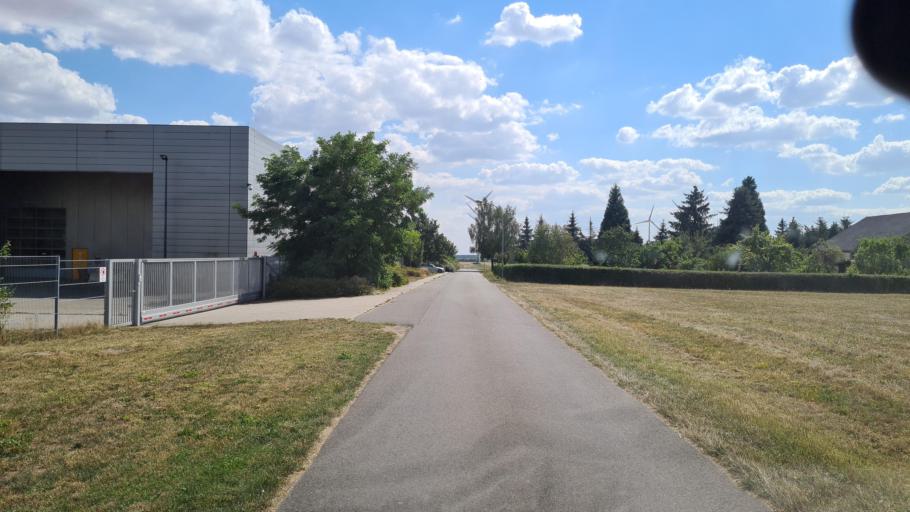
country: DE
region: Saxony-Anhalt
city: Kropstadt
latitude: 52.0110
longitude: 12.8214
